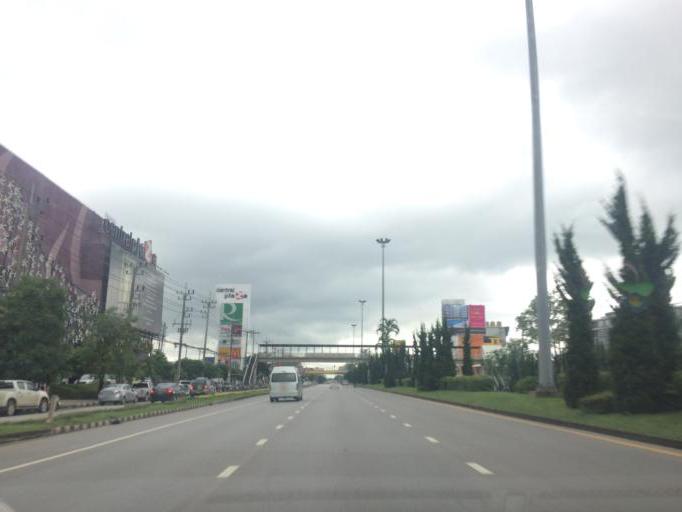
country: TH
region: Chiang Rai
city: Chiang Rai
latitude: 19.8854
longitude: 99.8351
